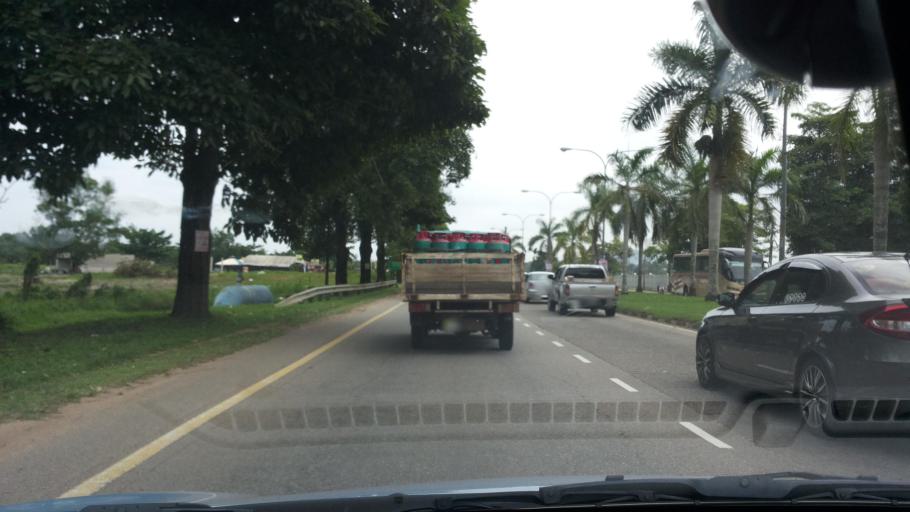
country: MY
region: Pahang
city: Kuantan
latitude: 3.7614
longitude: 103.2119
